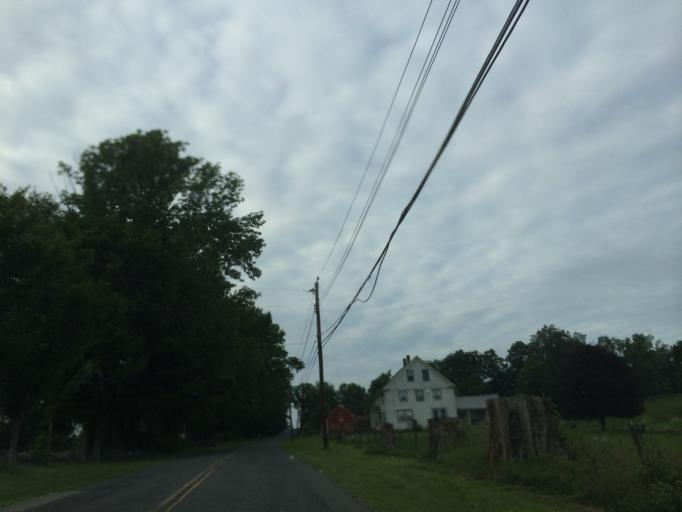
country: US
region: Massachusetts
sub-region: Berkshire County
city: Lanesborough
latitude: 42.5442
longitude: -73.2274
